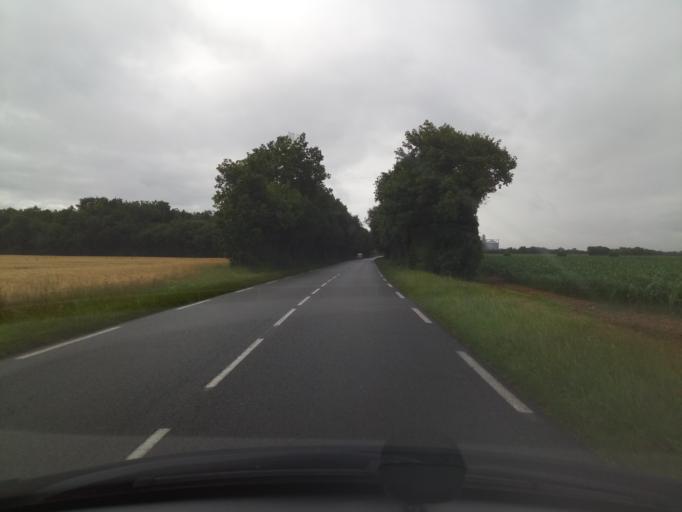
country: FR
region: Poitou-Charentes
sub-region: Departement de la Charente-Maritime
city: Courcon
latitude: 46.1812
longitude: -0.8527
